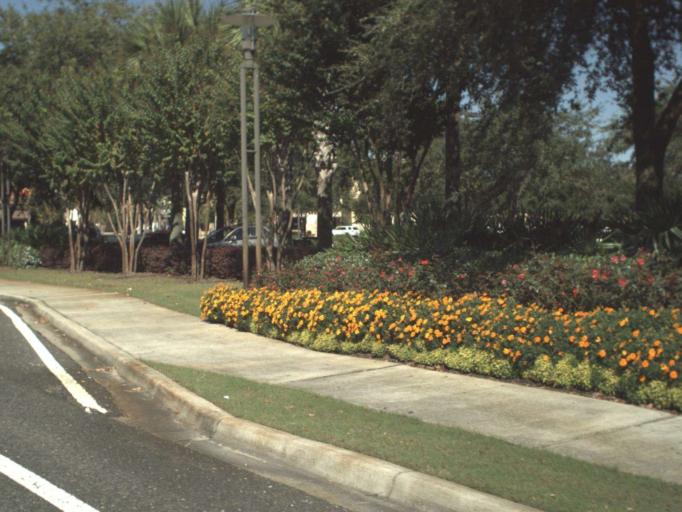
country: US
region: Florida
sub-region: Walton County
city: Miramar Beach
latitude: 30.3777
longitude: -86.3111
